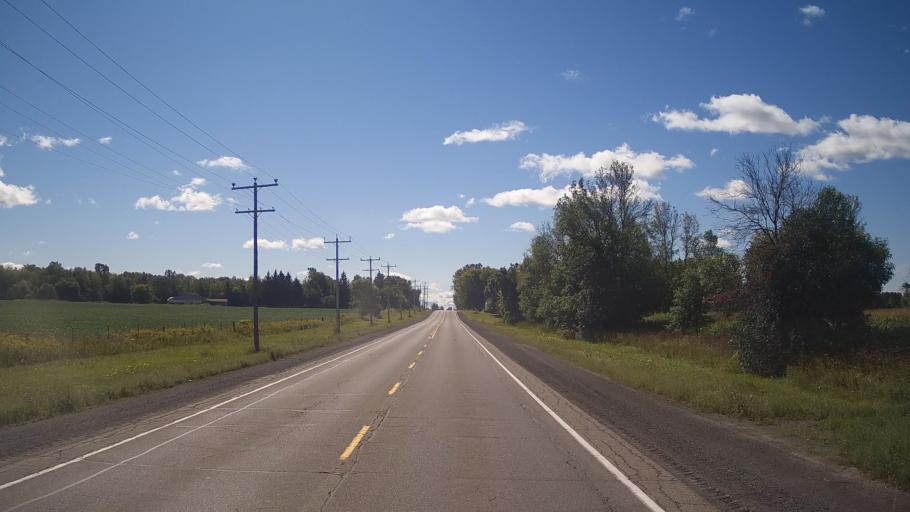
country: US
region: New York
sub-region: St. Lawrence County
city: Norfolk
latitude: 44.9629
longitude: -75.2340
